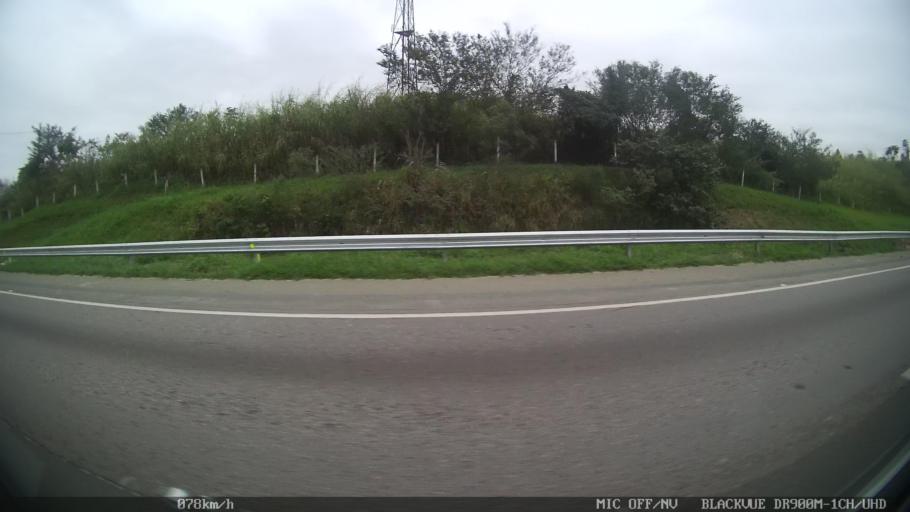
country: BR
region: Santa Catarina
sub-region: Barra Velha
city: Barra Velha
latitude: -26.5795
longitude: -48.7227
